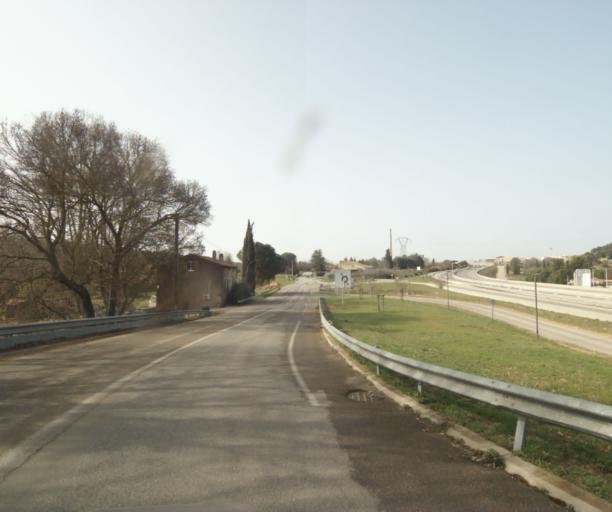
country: FR
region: Provence-Alpes-Cote d'Azur
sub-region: Departement des Bouches-du-Rhone
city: Meyreuil
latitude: 43.4737
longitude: 5.5169
